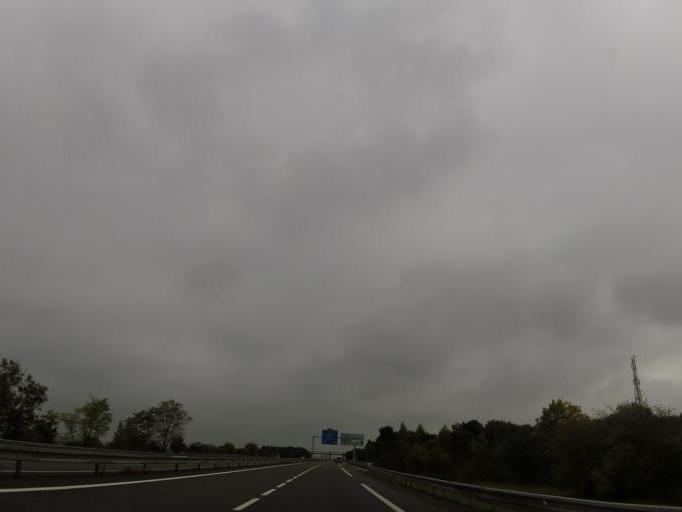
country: FR
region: Champagne-Ardenne
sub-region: Departement de la Marne
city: Saint-Memmie
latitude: 49.0354
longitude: 4.4334
